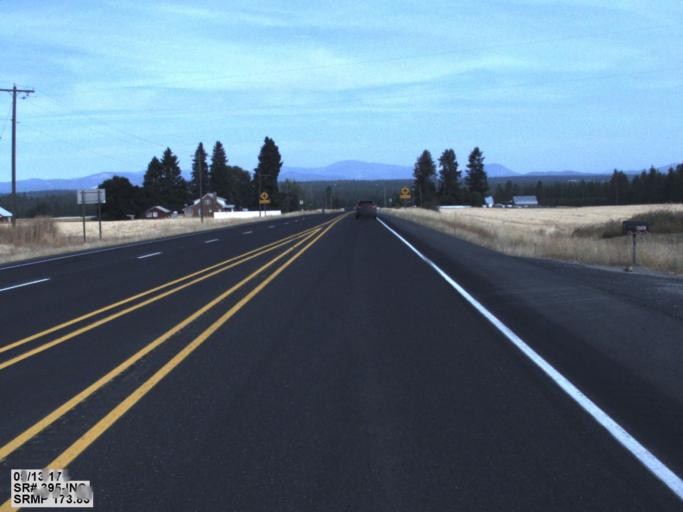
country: US
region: Washington
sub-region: Spokane County
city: Deer Park
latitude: 47.8704
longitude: -117.4220
